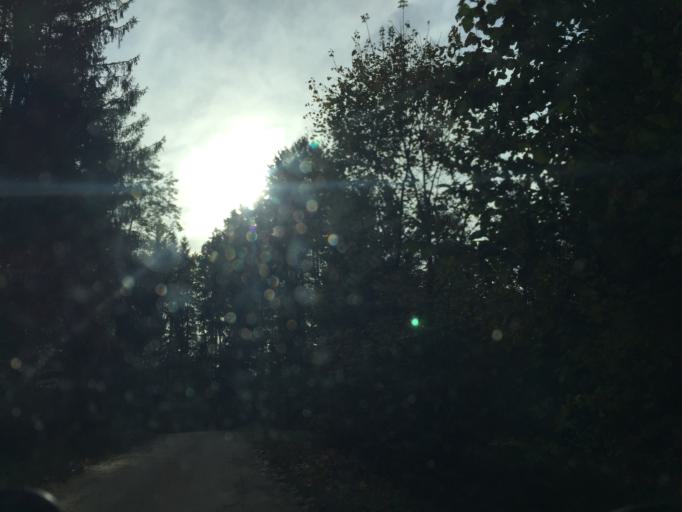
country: LV
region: Jaunpils
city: Jaunpils
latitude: 56.5898
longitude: 23.0090
